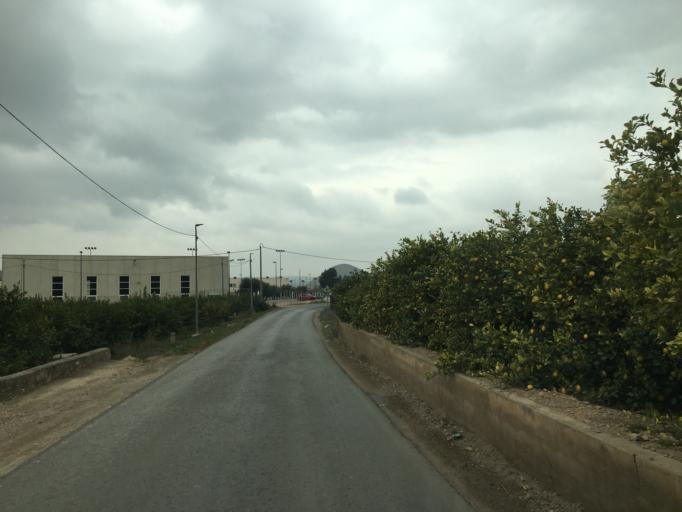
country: ES
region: Murcia
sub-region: Murcia
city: Santomera
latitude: 38.0803
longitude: -1.0508
